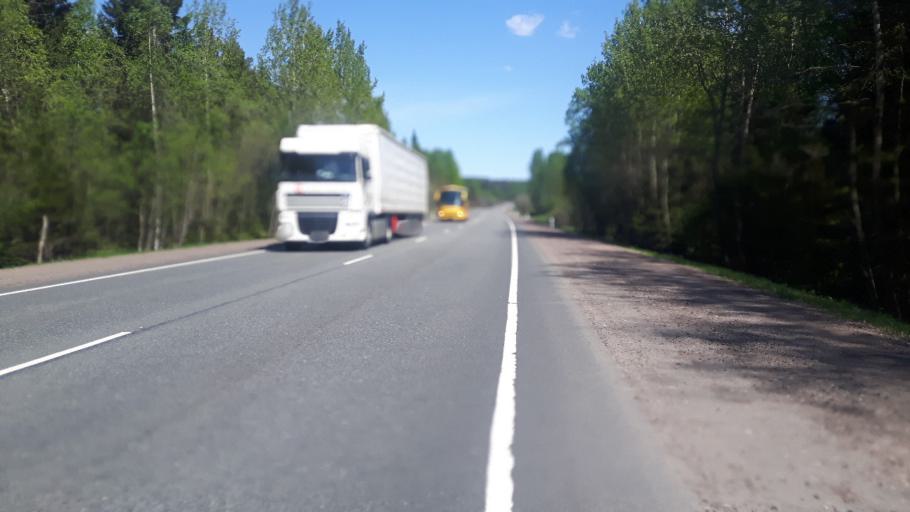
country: RU
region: Leningrad
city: Vysotsk
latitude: 60.6292
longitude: 28.2659
